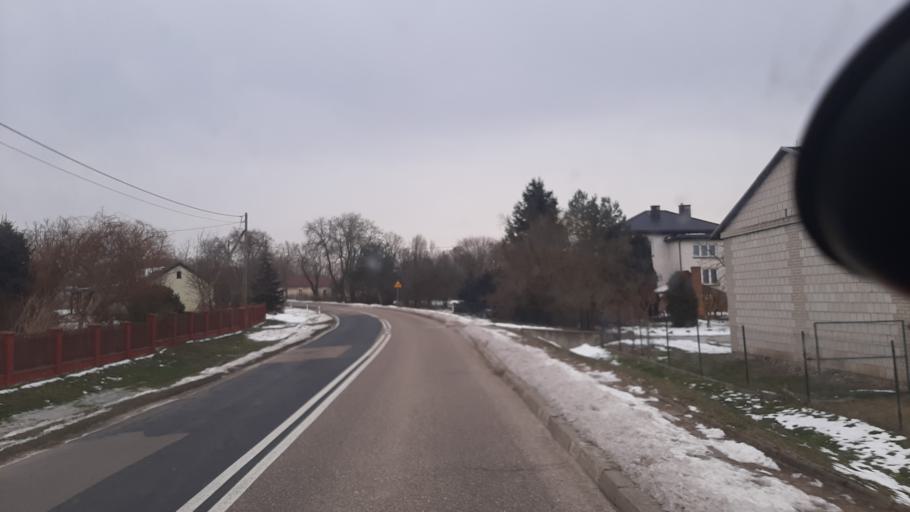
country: PL
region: Lublin Voivodeship
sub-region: Powiat lubartowski
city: Kamionka
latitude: 51.4489
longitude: 22.4216
